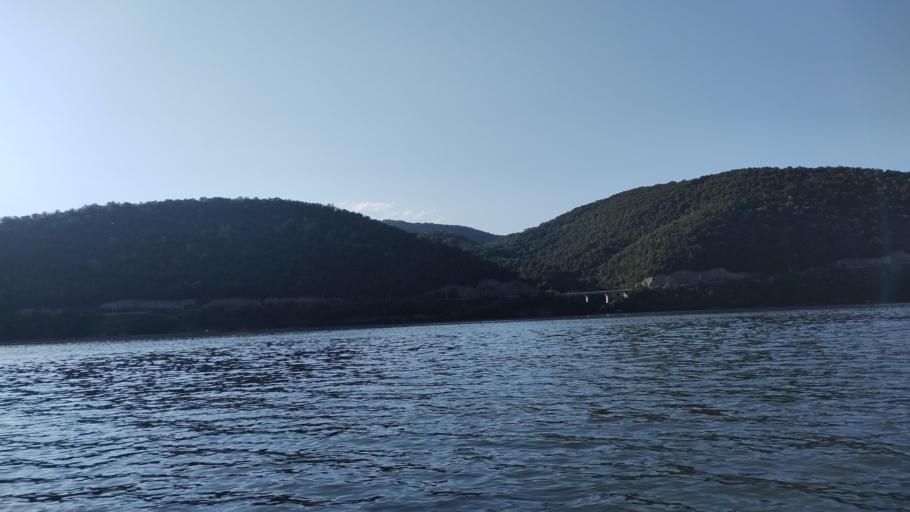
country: RO
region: Mehedinti
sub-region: Comuna Dubova
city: Dubova
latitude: 44.5808
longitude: 22.2491
